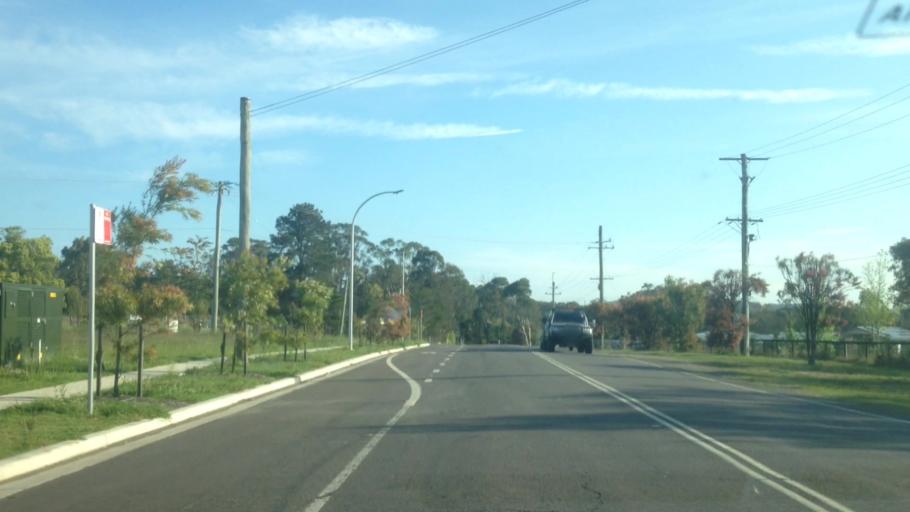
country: AU
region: New South Wales
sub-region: Lake Macquarie Shire
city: Dora Creek
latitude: -33.1053
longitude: 151.4770
